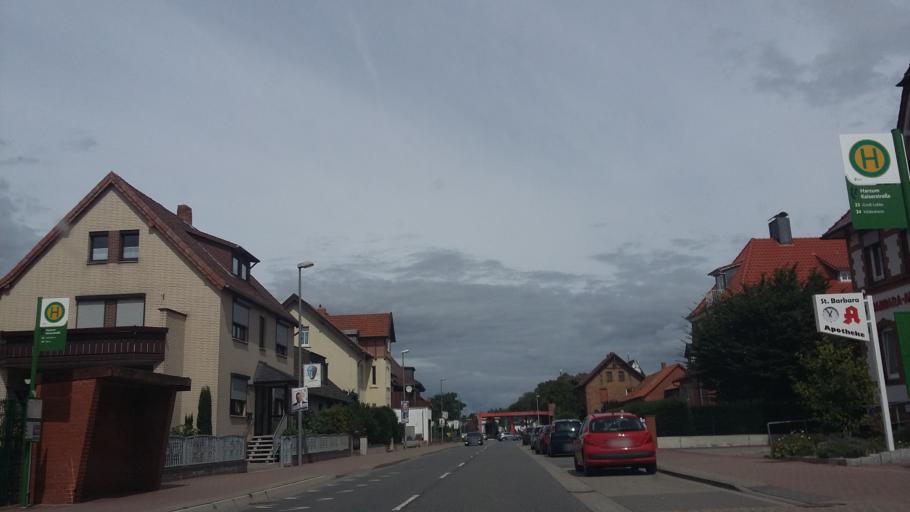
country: DE
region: Lower Saxony
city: Harsum
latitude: 52.2092
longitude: 9.9648
